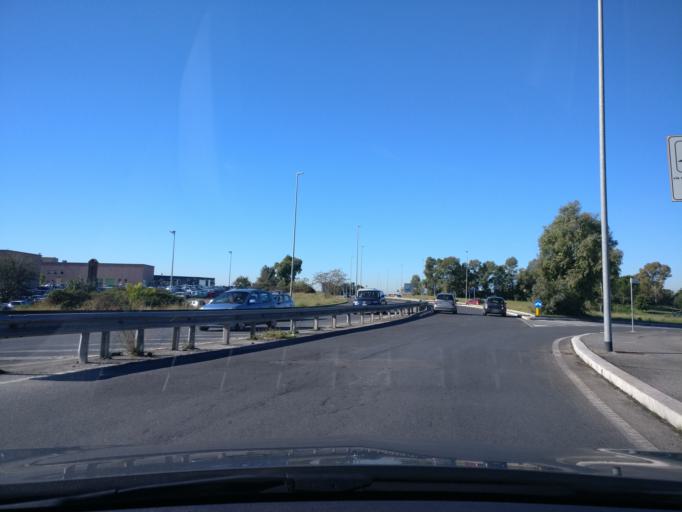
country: IT
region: Latium
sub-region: Citta metropolitana di Roma Capitale
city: Frascati
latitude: 41.8569
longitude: 12.6244
